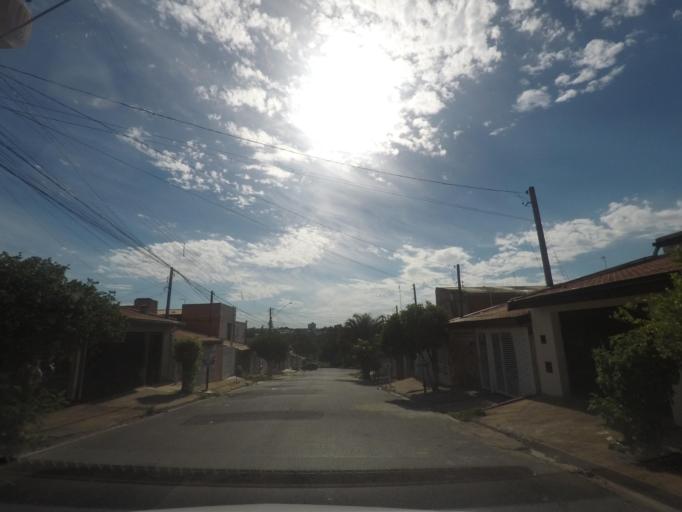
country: BR
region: Sao Paulo
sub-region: Sumare
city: Sumare
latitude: -22.8089
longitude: -47.2722
